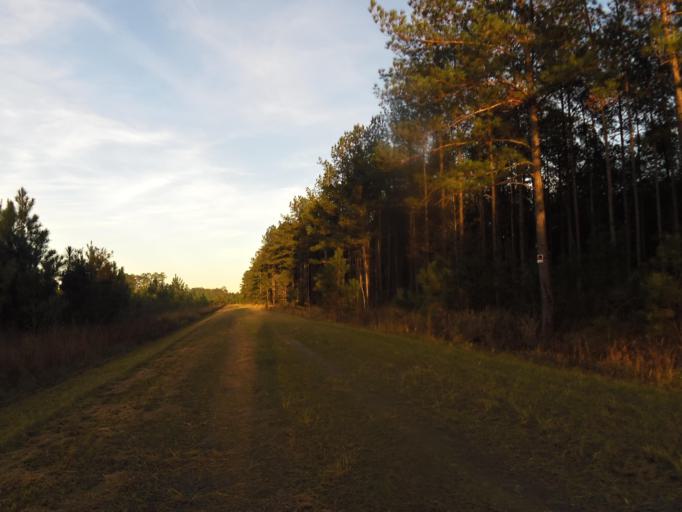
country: US
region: Florida
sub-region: Putnam County
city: Palatka
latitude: 29.6798
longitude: -81.7446
